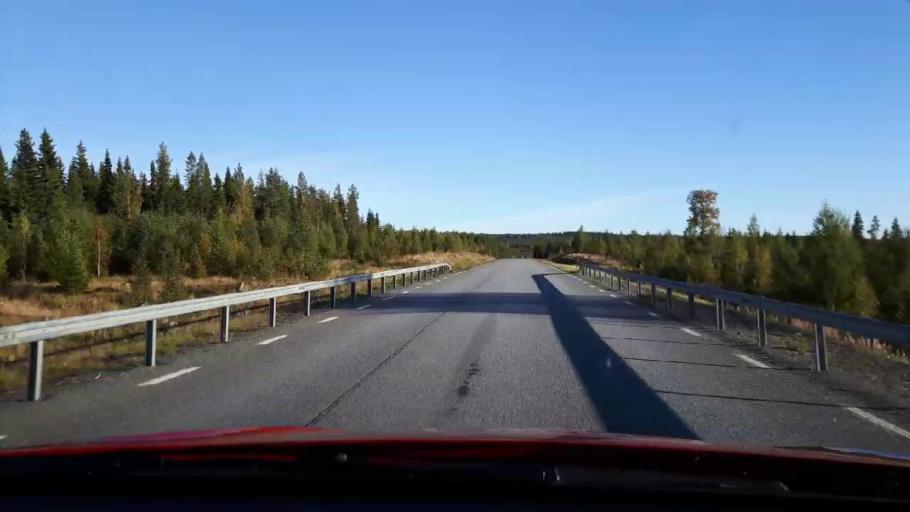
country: SE
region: Jaemtland
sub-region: OEstersunds Kommun
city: Lit
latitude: 63.7731
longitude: 14.7150
